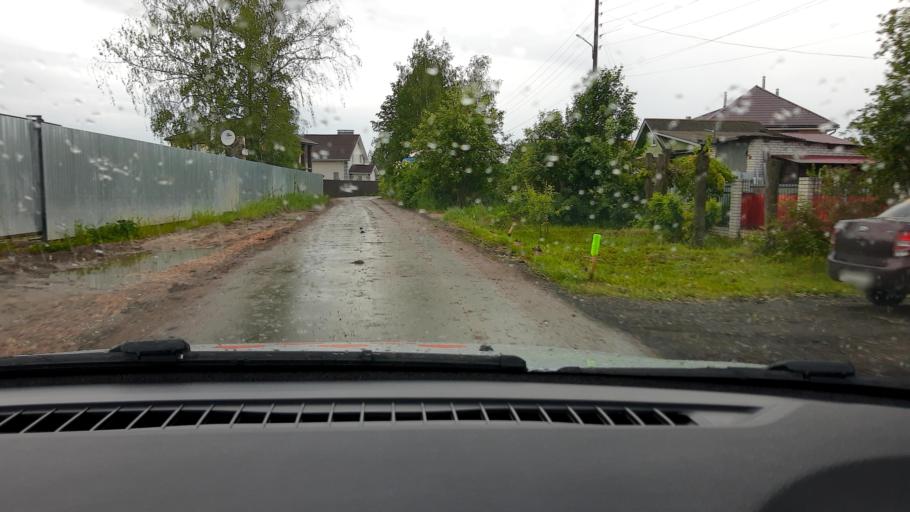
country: RU
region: Nizjnij Novgorod
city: Gorbatovka
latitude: 56.2354
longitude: 43.7358
